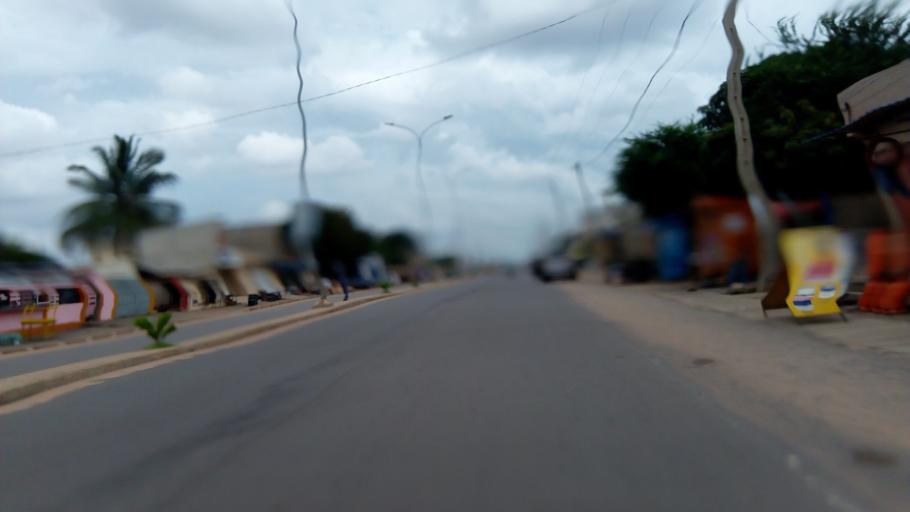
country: TG
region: Maritime
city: Lome
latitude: 6.2079
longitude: 1.1815
